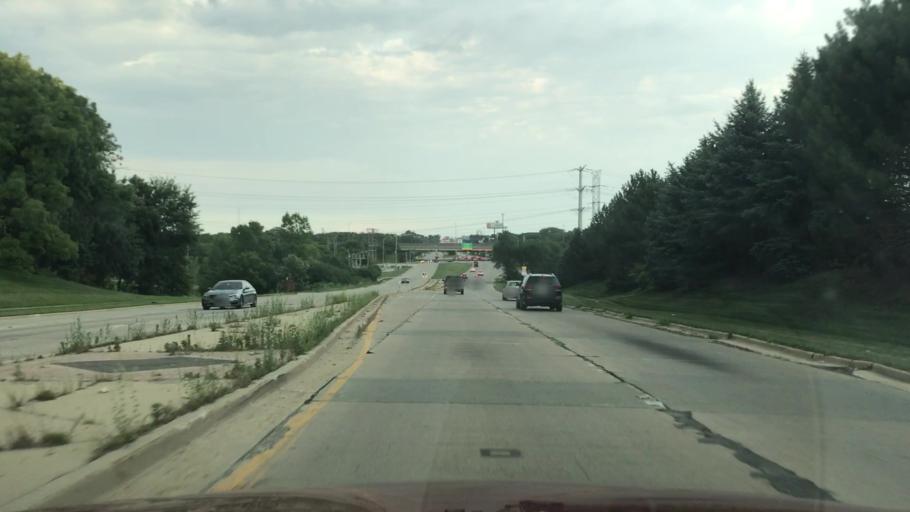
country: US
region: Illinois
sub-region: DuPage County
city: Glen Ellyn
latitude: 41.8595
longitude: -88.0480
